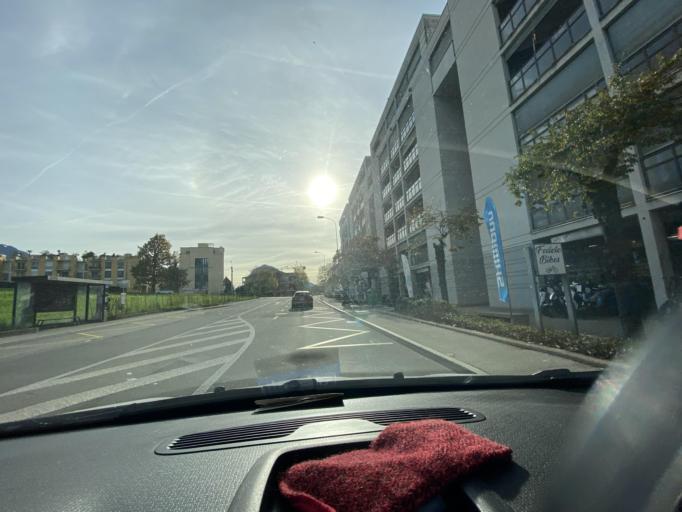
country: CH
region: Ticino
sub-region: Lugano District
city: Viganello
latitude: 46.0210
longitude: 8.9657
